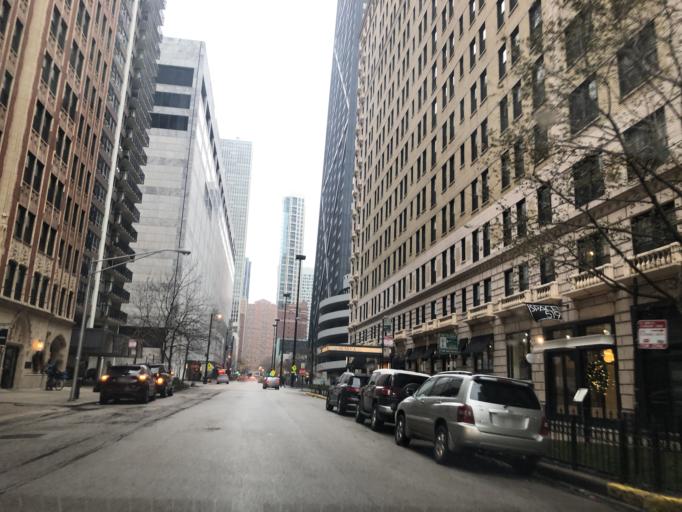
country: US
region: Illinois
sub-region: Cook County
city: Chicago
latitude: 41.8984
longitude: -87.6208
